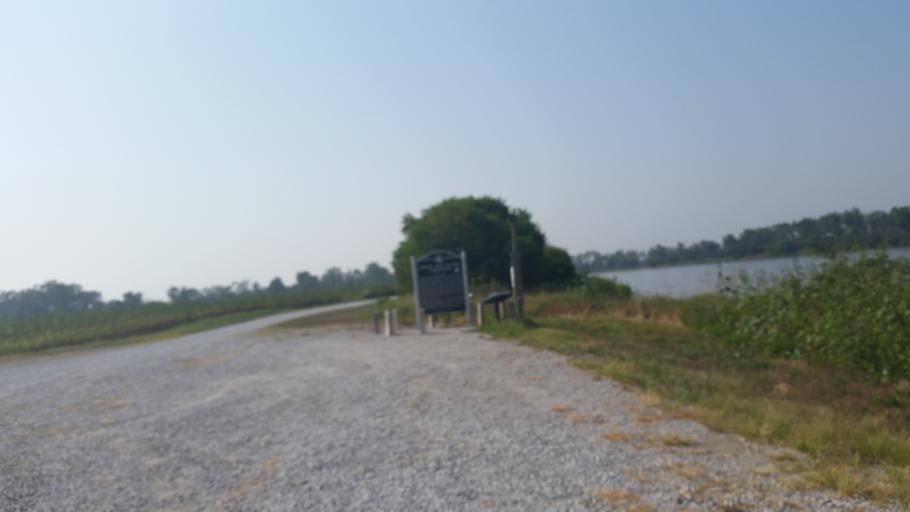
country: US
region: Nebraska
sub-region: Cass County
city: Plattsmouth
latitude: 41.0519
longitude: -95.8825
